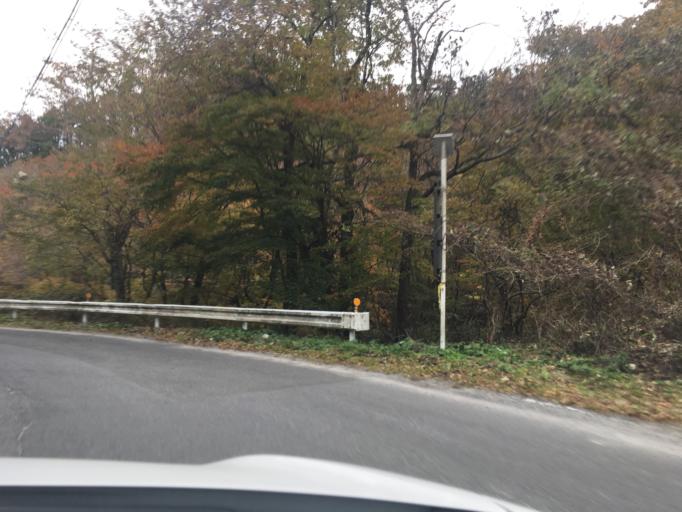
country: JP
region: Fukushima
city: Iwaki
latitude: 37.2079
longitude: 140.6956
